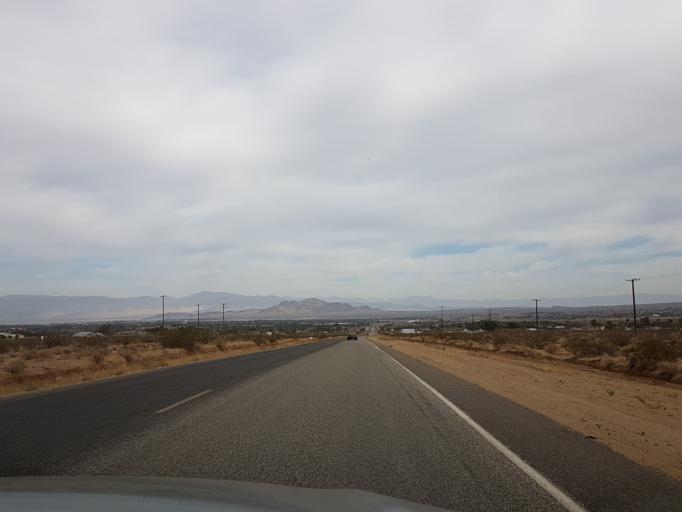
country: US
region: California
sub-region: Kern County
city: Ridgecrest
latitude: 35.5847
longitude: -117.7047
